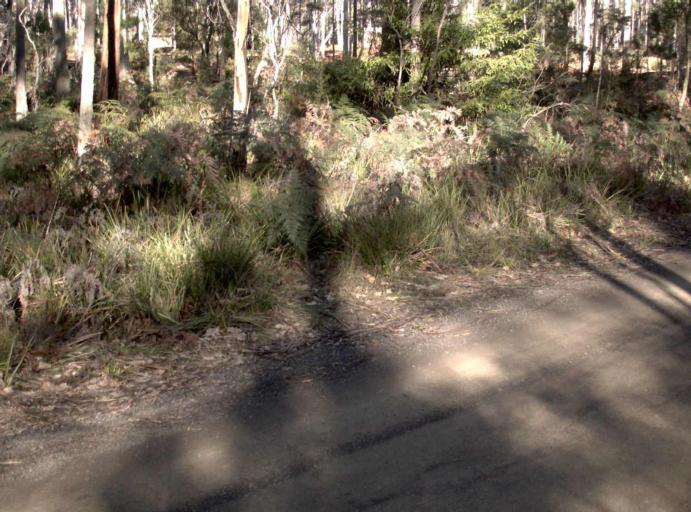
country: AU
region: Tasmania
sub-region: Launceston
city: Mayfield
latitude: -41.3091
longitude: 147.2063
